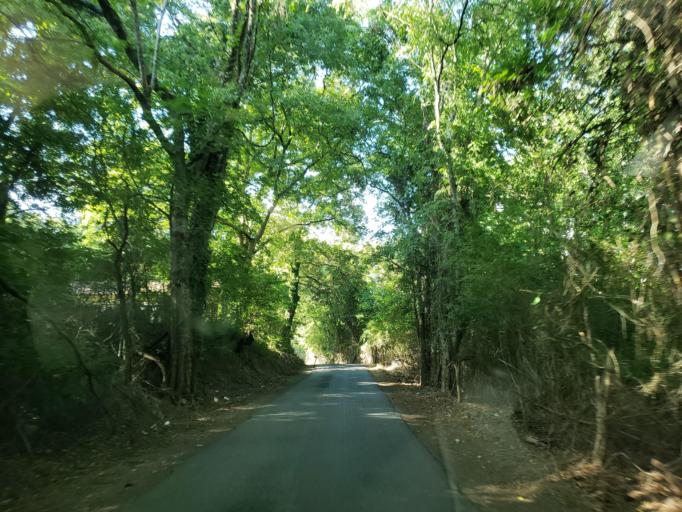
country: US
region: Georgia
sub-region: Floyd County
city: Lindale
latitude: 34.2130
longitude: -85.1267
